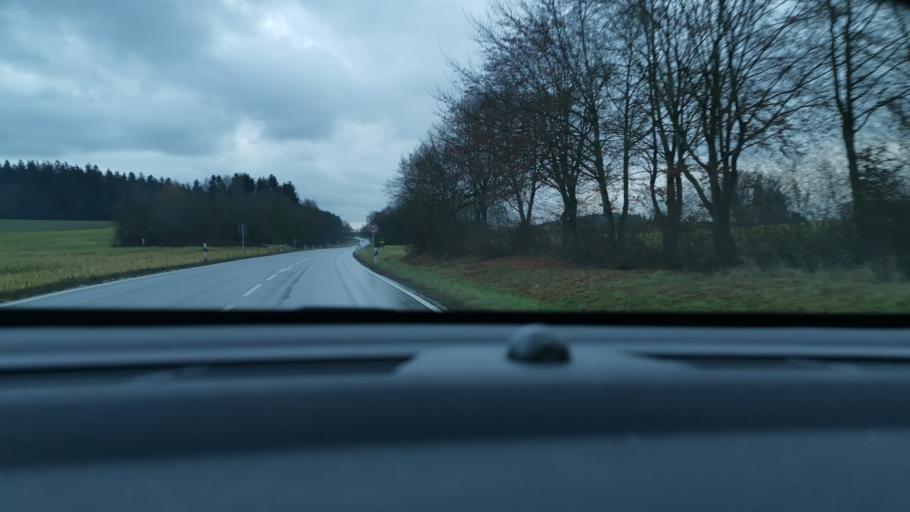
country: DE
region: Bavaria
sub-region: Swabia
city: Affing
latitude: 48.4823
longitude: 11.0051
